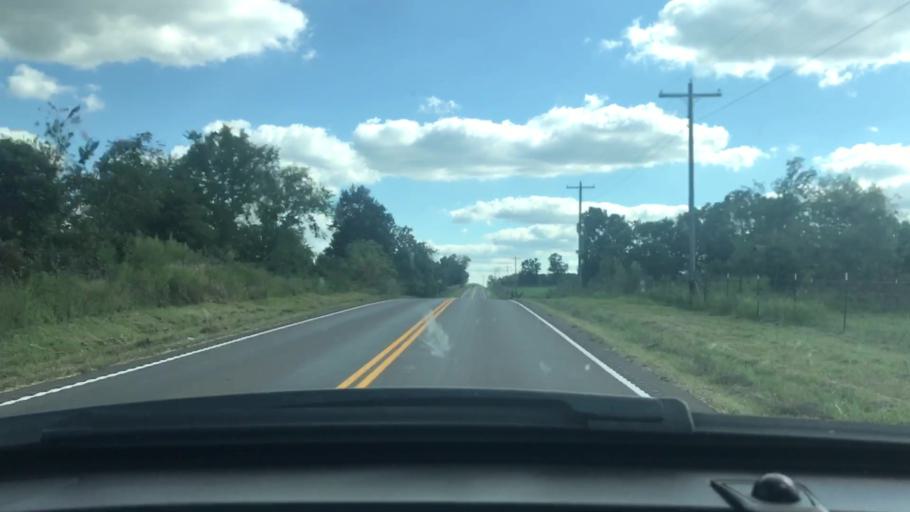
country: US
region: Missouri
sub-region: Wright County
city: Mountain Grove
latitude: 37.2400
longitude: -92.3005
